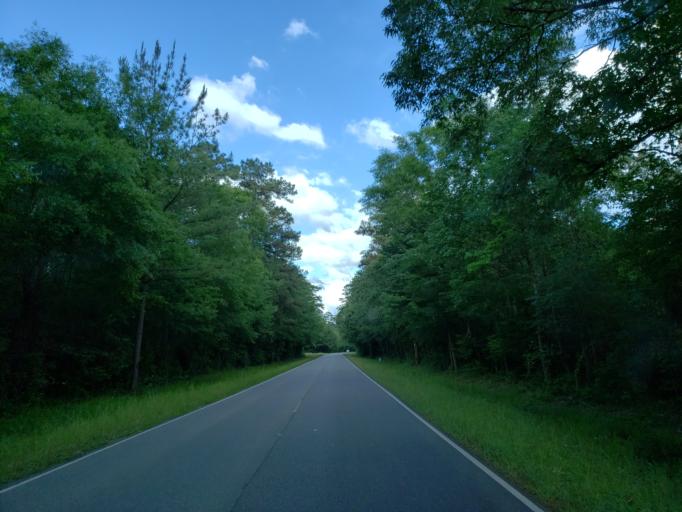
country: US
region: Mississippi
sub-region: Forrest County
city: Petal
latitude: 31.3107
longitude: -89.2304
